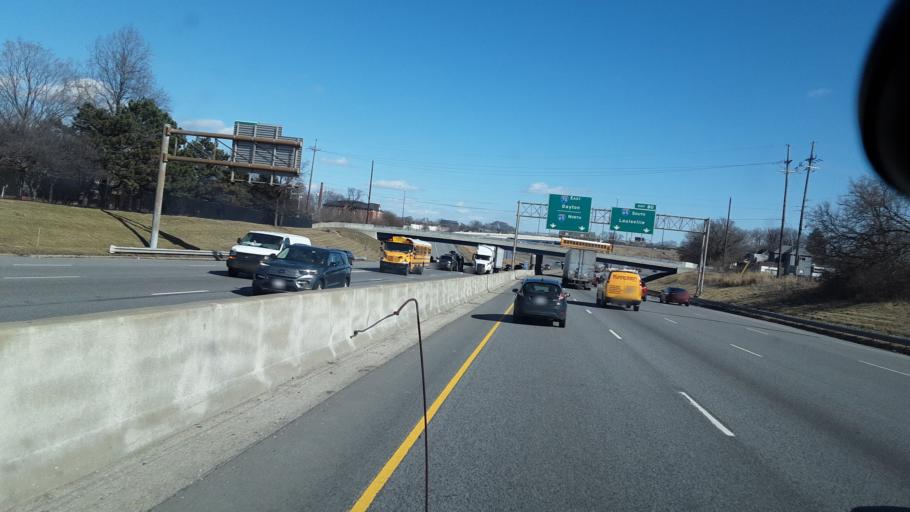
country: US
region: Indiana
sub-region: Marion County
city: Indianapolis
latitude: 39.7530
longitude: -86.1536
